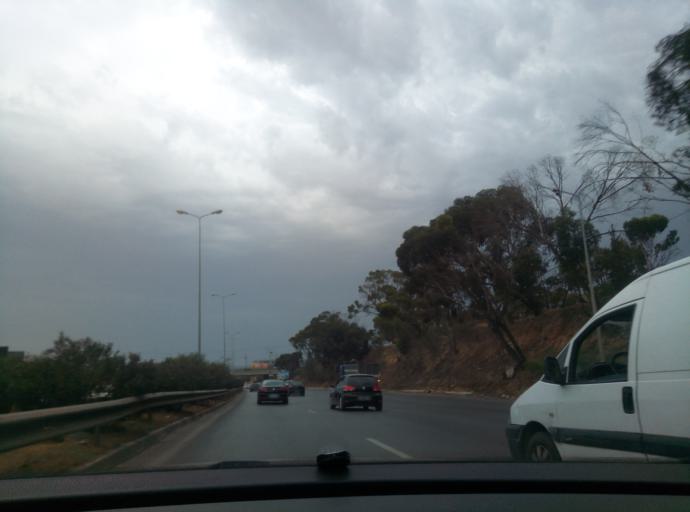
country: TN
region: Bin 'Arus
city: Ben Arous
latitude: 36.7400
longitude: 10.2160
